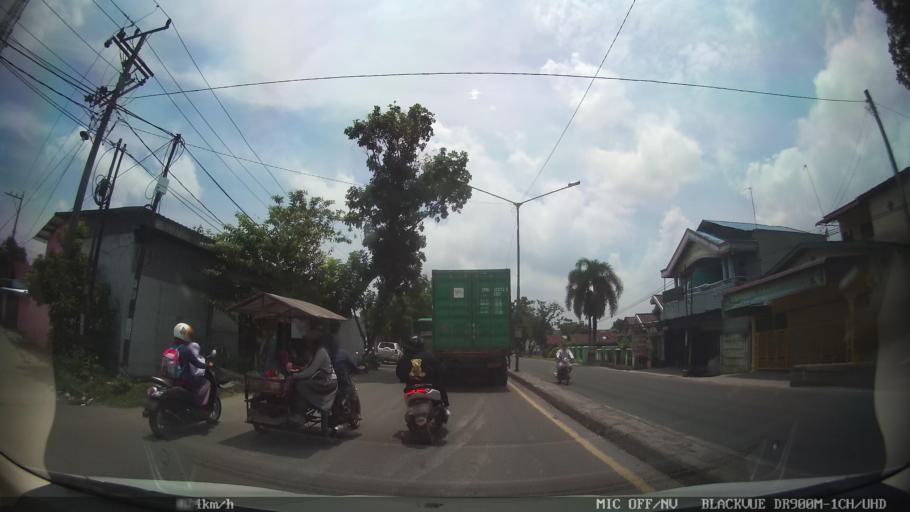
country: ID
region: North Sumatra
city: Labuhan Deli
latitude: 3.7107
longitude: 98.6797
